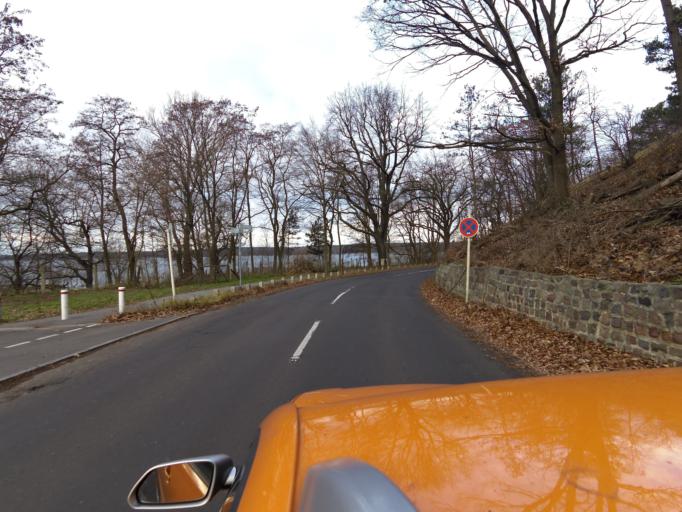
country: DE
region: Berlin
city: Nikolassee
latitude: 52.4548
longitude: 13.1896
